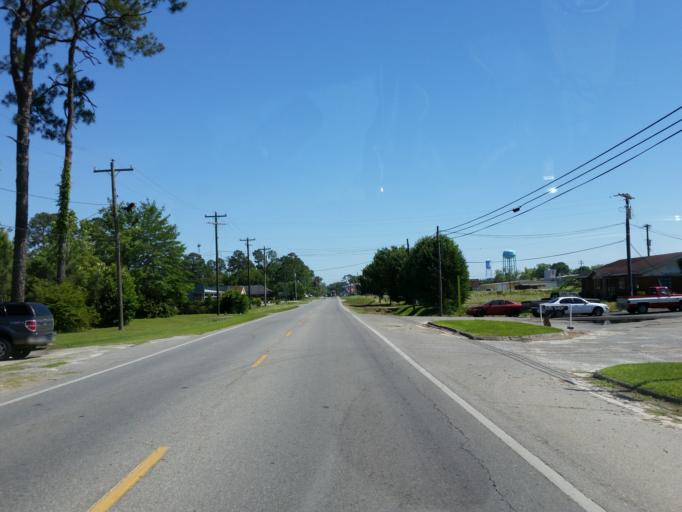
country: US
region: Georgia
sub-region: Cook County
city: Adel
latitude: 31.1471
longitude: -83.4270
